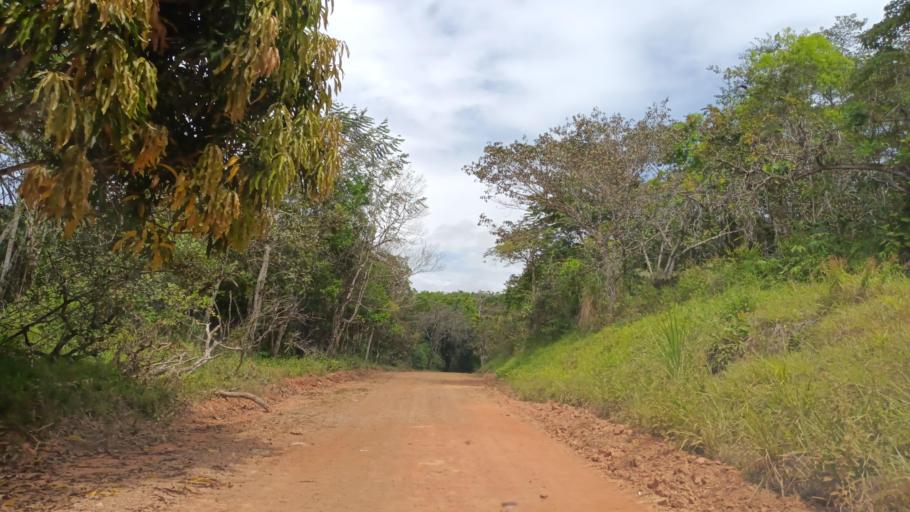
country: PA
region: Panama
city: La Cabima
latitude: 9.1292
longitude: -79.5040
